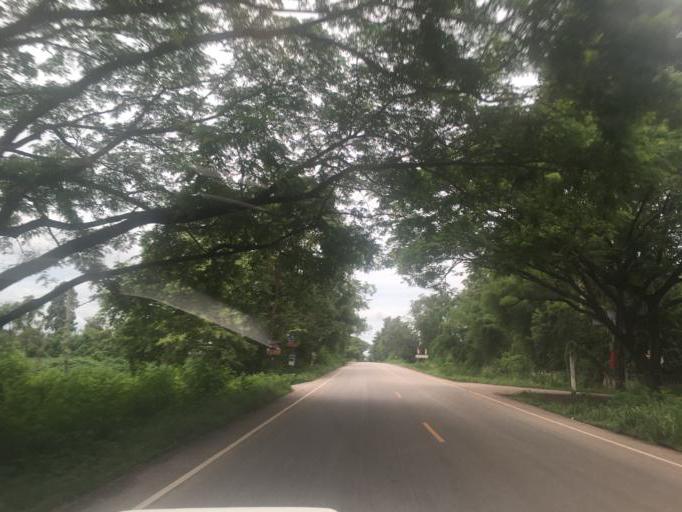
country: TH
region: Changwat Udon Thani
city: Udon Thani
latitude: 17.3220
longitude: 102.7127
